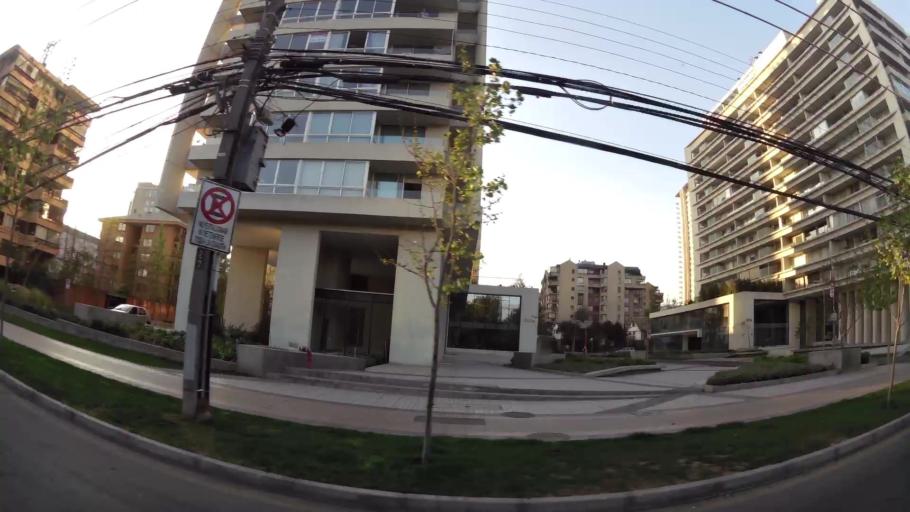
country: CL
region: Santiago Metropolitan
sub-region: Provincia de Santiago
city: Villa Presidente Frei, Nunoa, Santiago, Chile
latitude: -33.4014
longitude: -70.5733
